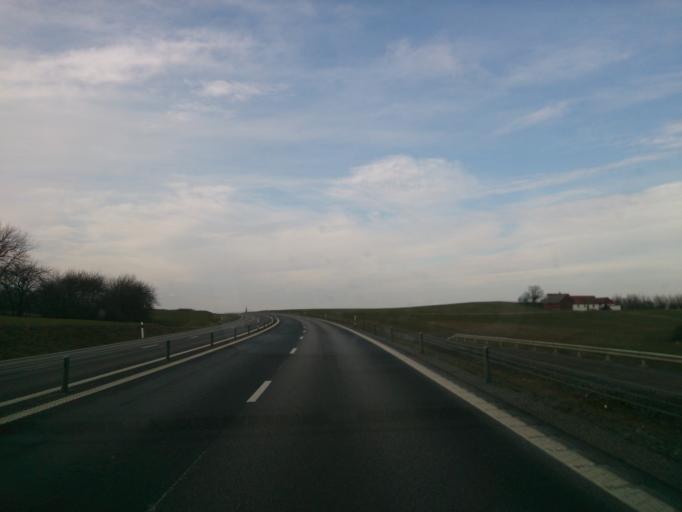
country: SE
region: Skane
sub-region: Svedala Kommun
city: Klagerup
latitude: 55.5686
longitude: 13.2561
